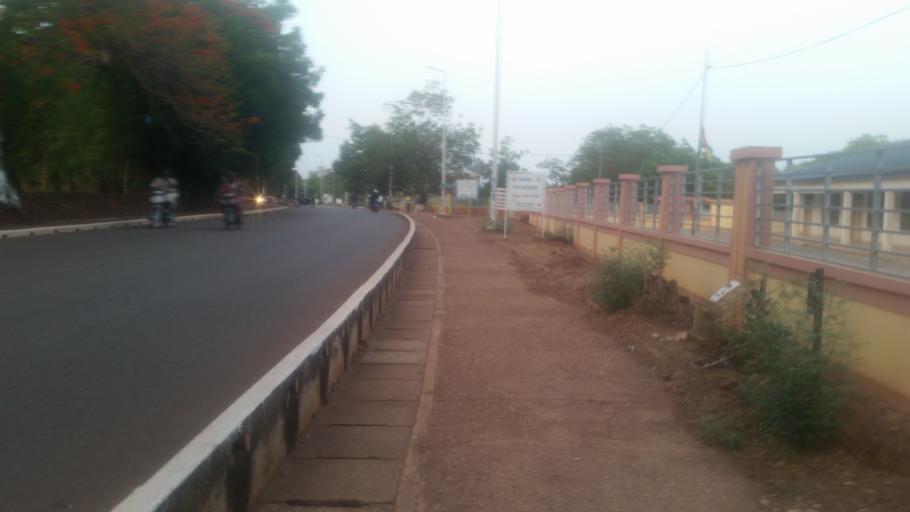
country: GH
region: Northern
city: Tamale
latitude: 9.4049
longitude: -0.8327
